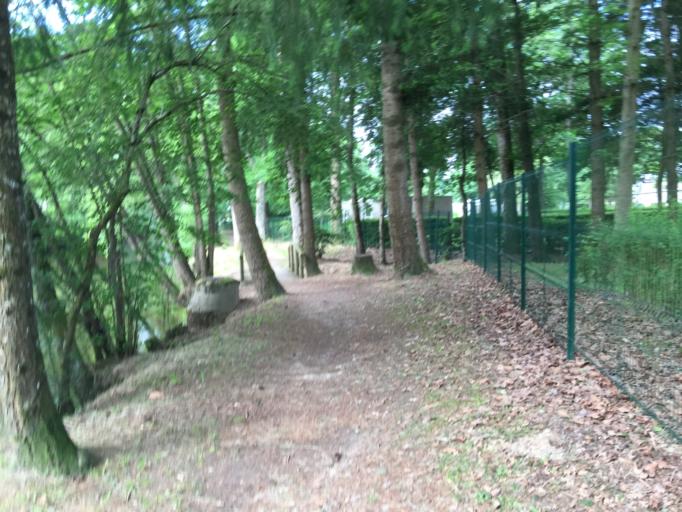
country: FR
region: Auvergne
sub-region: Departement du Puy-de-Dome
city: Ambert
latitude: 45.5399
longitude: 3.7303
